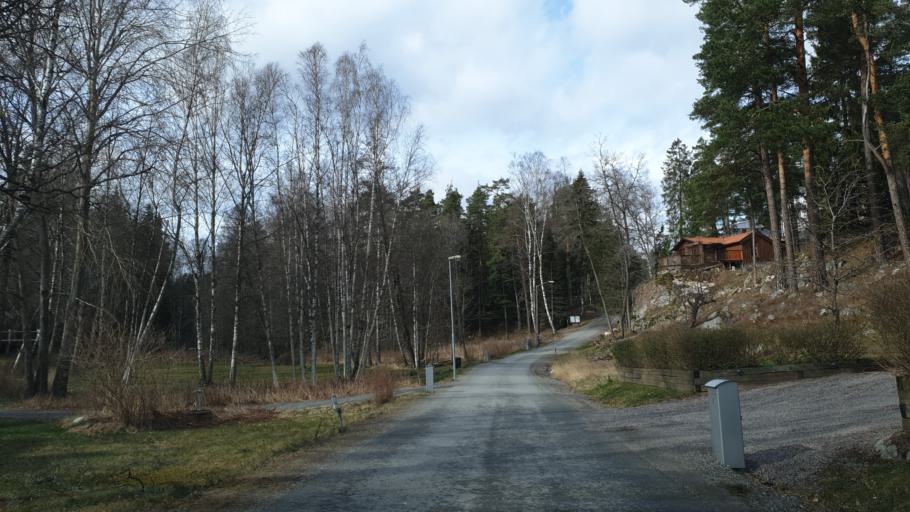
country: SE
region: Stockholm
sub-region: Nacka Kommun
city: Boo
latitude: 59.3298
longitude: 18.2928
